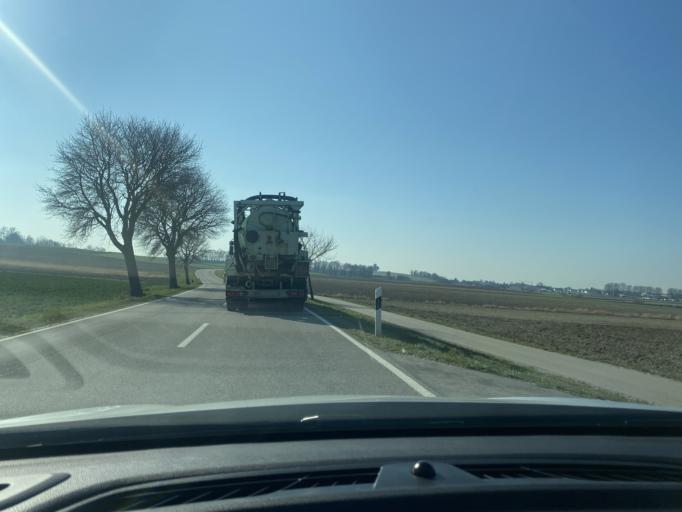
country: DE
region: Bavaria
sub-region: Upper Bavaria
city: Oberding
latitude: 48.2969
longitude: 11.8479
